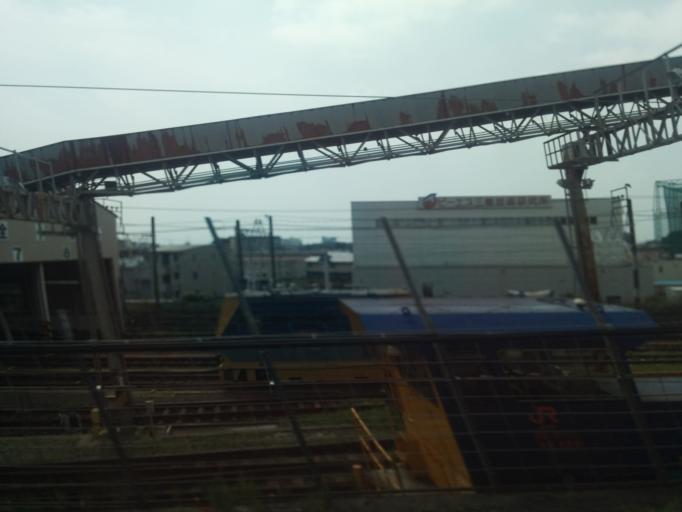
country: JP
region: Kanagawa
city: Odawara
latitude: 35.2740
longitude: 139.1728
